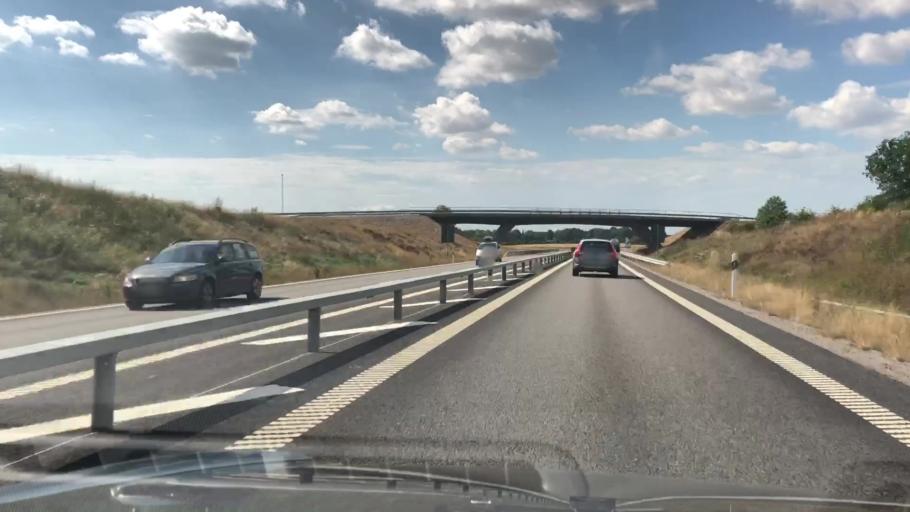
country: SE
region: Kalmar
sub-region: Kalmar Kommun
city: Rinkabyholm
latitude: 56.6497
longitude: 16.2389
